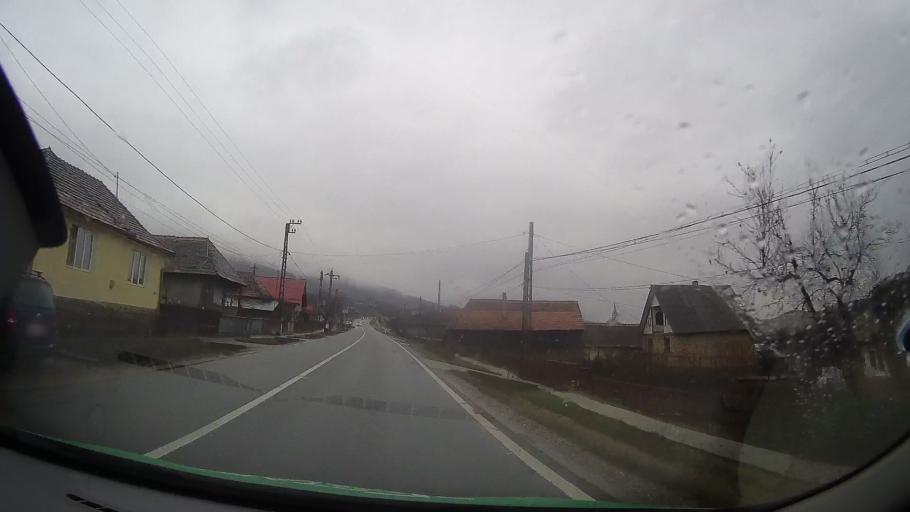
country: RO
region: Bistrita-Nasaud
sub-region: Comuna Galatii Bistritei
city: Galatii Bistritei
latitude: 46.9953
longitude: 24.4161
